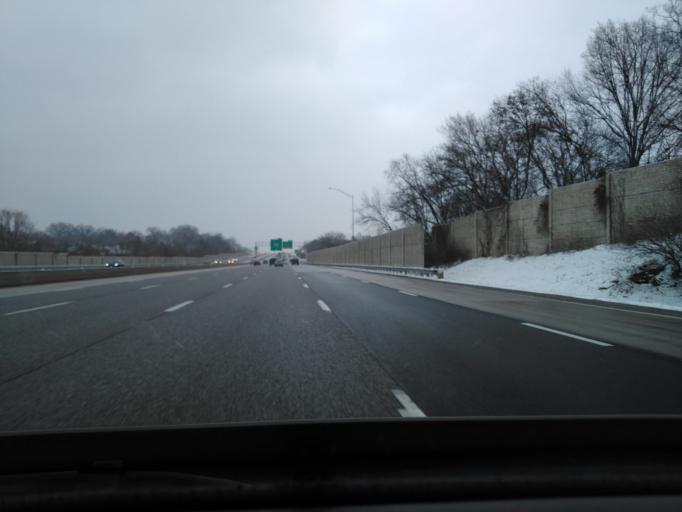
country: US
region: Missouri
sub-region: Saint Louis County
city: Concord
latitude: 38.5117
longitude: -90.3667
